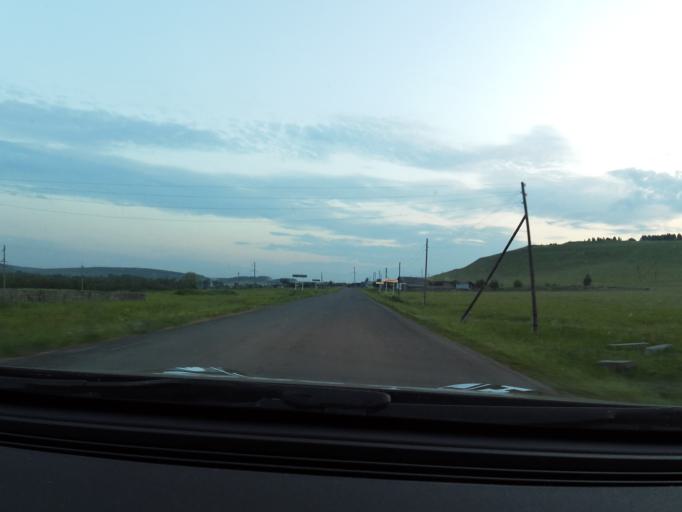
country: RU
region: Sverdlovsk
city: Arti
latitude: 56.1873
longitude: 58.3323
